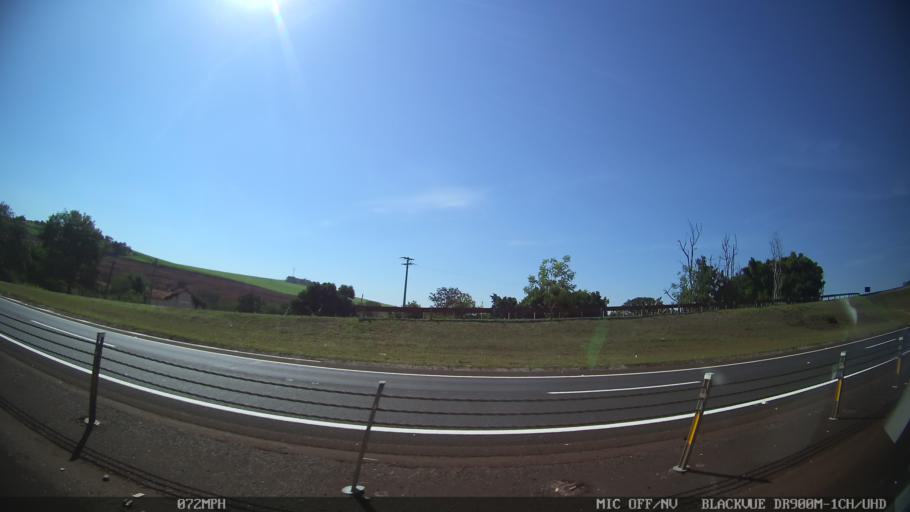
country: BR
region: Sao Paulo
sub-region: Ribeirao Preto
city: Ribeirao Preto
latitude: -21.1975
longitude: -47.8780
